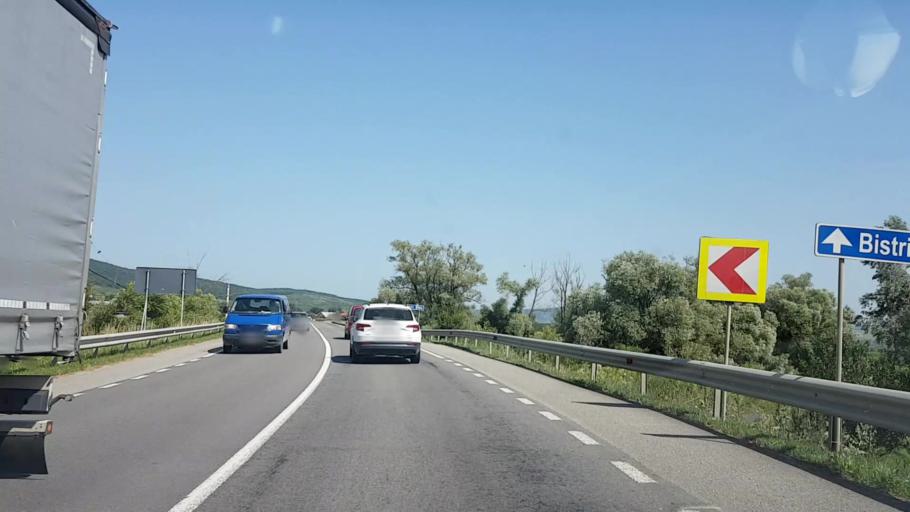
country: RO
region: Bistrita-Nasaud
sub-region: Comuna Sintereag
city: Sintereag
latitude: 47.1798
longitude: 24.2711
